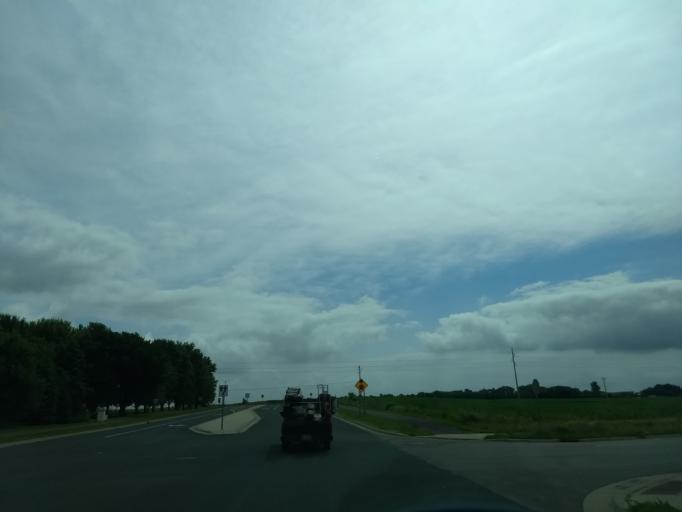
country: US
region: Minnesota
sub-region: Dakota County
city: Rosemount
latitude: 44.7427
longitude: -93.0880
